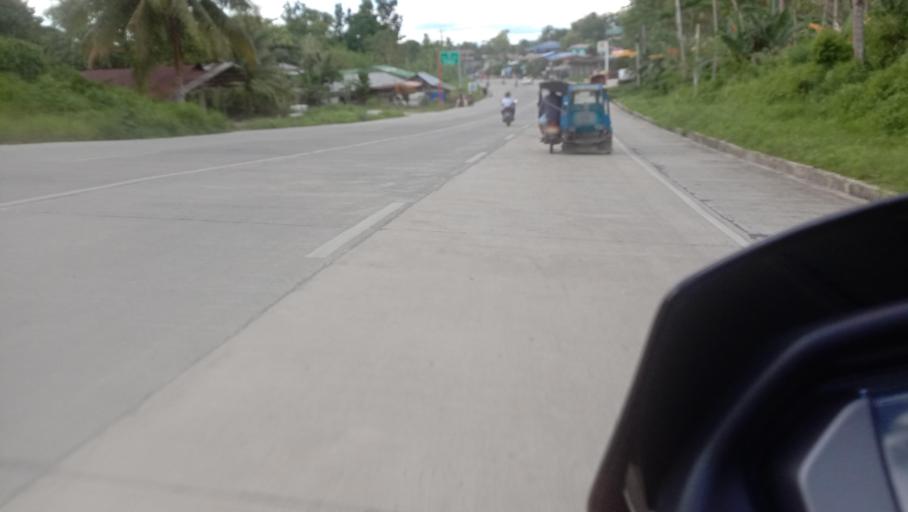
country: PH
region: Caraga
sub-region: Province of Surigao del Sur
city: Barobo
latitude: 8.5246
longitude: 126.1194
